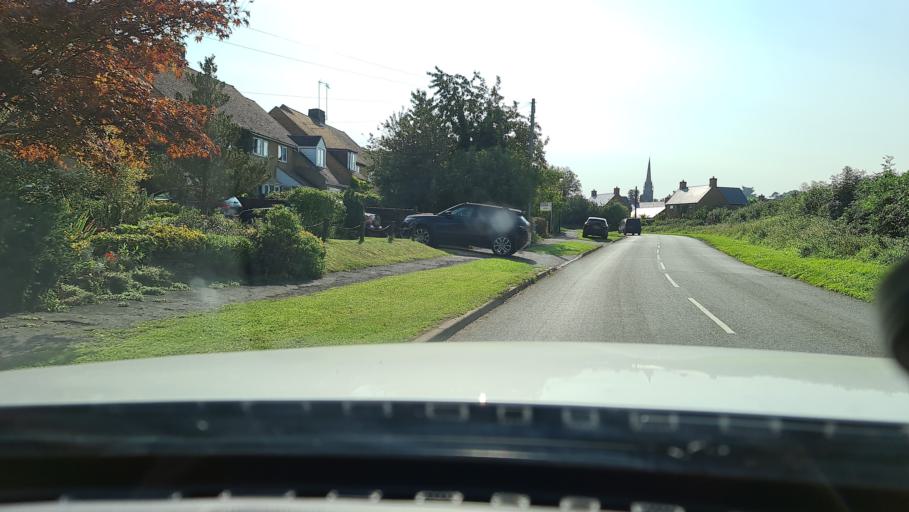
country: GB
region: England
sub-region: Oxfordshire
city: Adderbury
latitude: 52.0264
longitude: -1.2792
